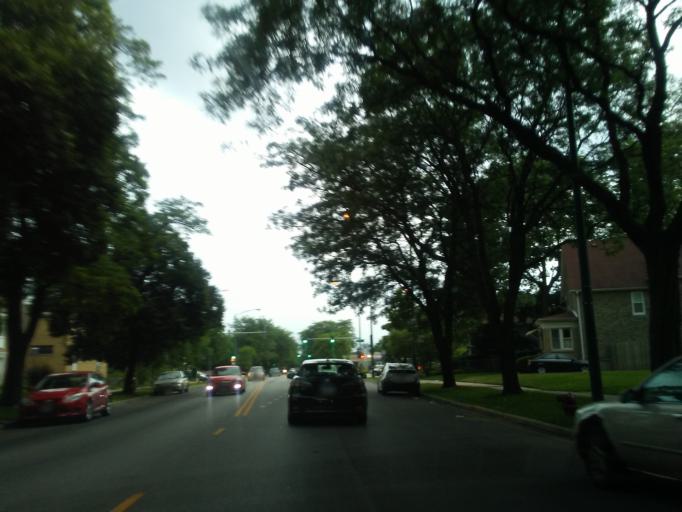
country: US
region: Illinois
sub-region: Cook County
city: Evanston
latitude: 42.0060
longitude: -87.6806
